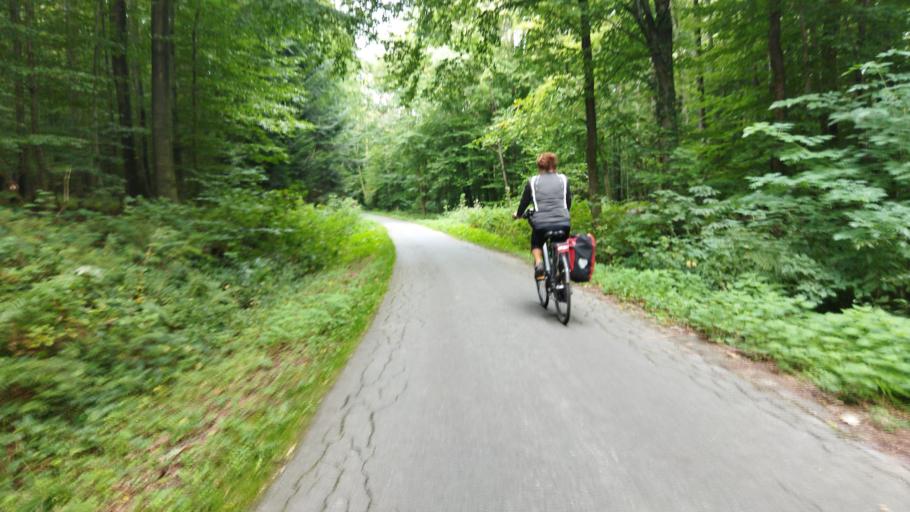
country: DE
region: Lower Saxony
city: Bad Iburg
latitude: 52.1593
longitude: 8.0748
